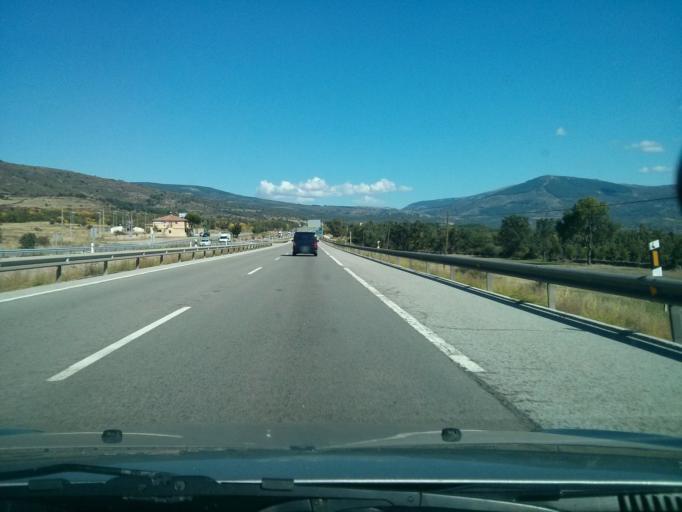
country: ES
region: Madrid
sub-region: Provincia de Madrid
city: Braojos
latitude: 41.0438
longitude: -3.6163
